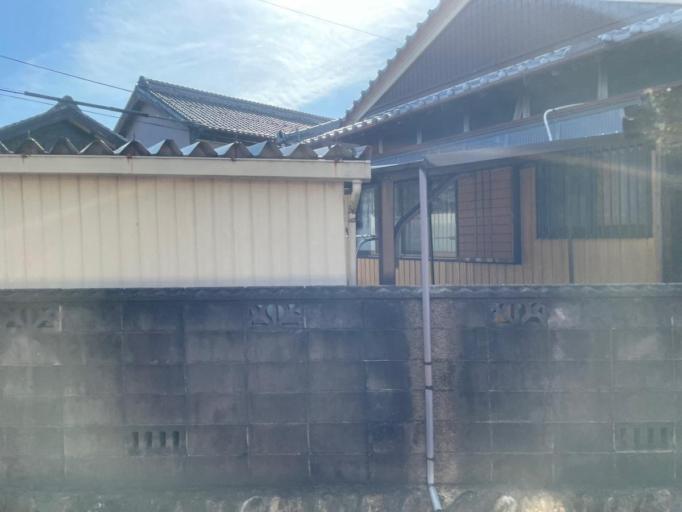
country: JP
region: Mie
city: Yokkaichi
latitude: 34.9760
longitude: 136.5760
